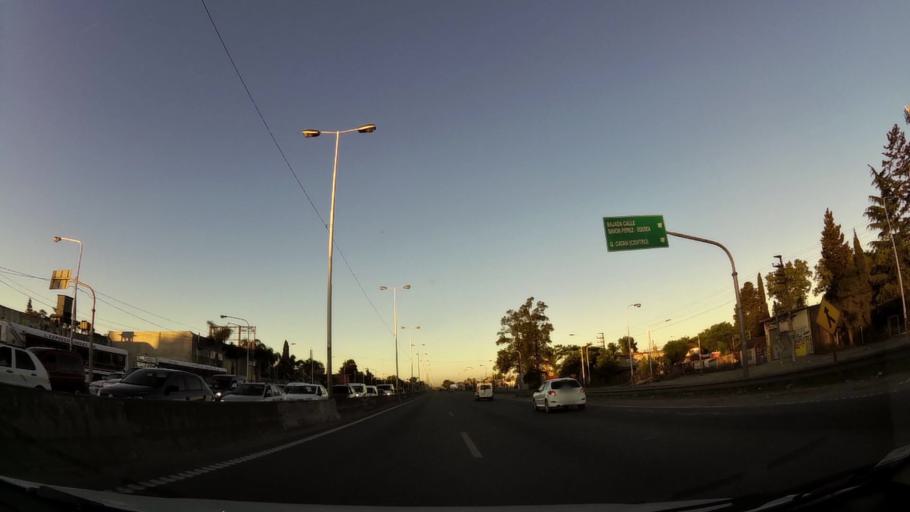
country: AR
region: Buenos Aires
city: Pontevedra
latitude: -34.7931
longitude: -58.6318
